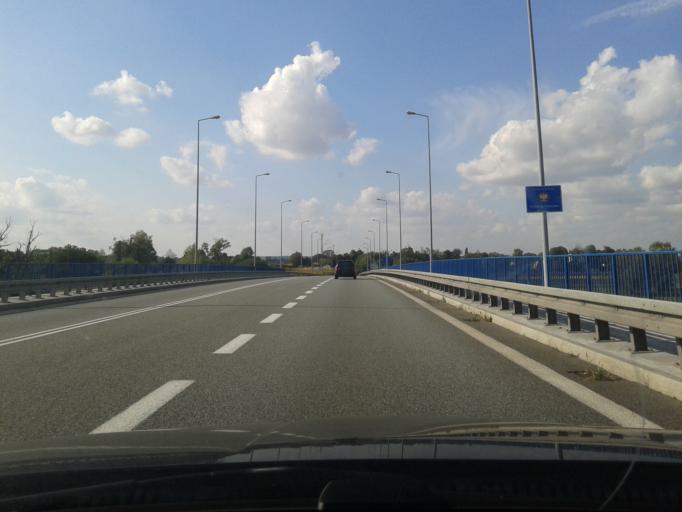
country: PL
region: Silesian Voivodeship
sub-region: Powiat raciborski
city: Chalupki
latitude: 49.9168
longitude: 18.3230
